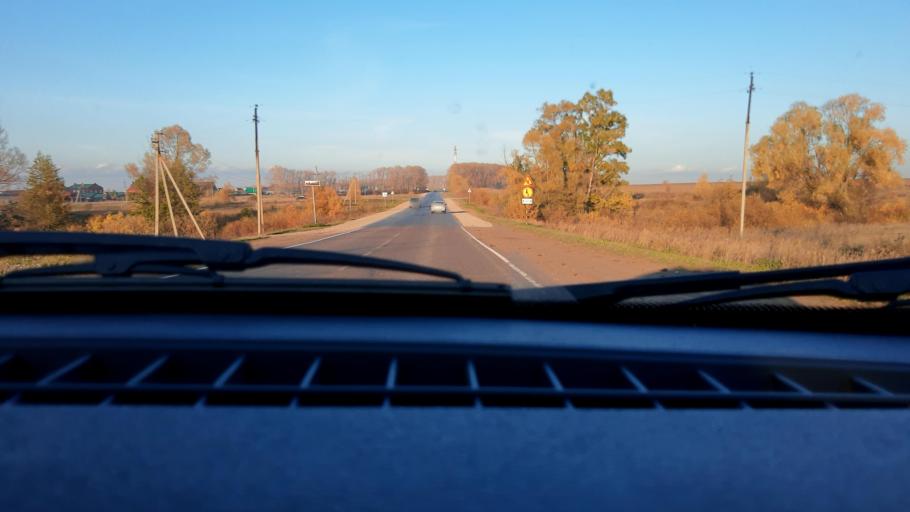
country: RU
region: Bashkortostan
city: Asanovo
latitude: 54.8117
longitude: 55.5785
